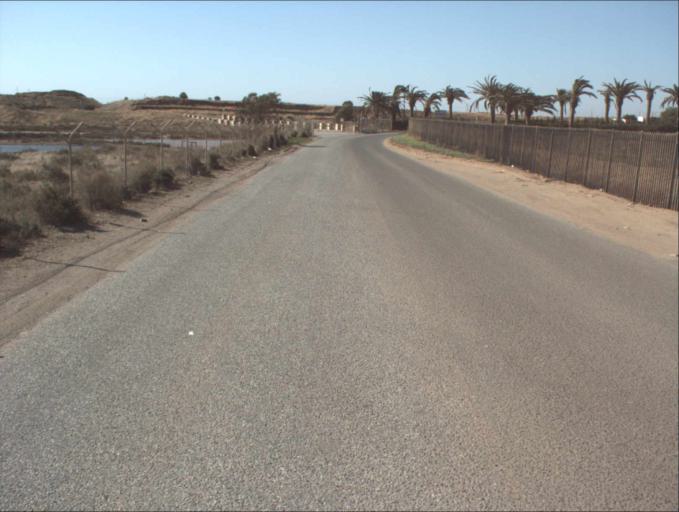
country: AU
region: South Australia
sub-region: Port Adelaide Enfield
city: Alberton
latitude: -34.8310
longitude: 138.5459
